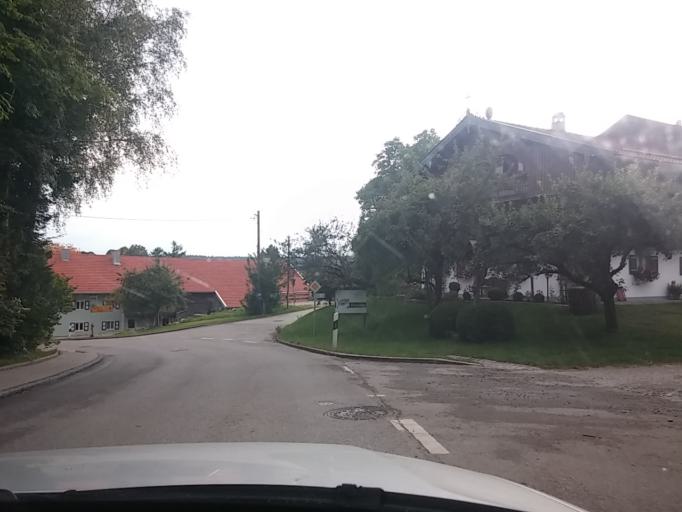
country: DE
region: Bavaria
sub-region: Upper Bavaria
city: Reichertshausen
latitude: 47.8902
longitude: 11.5879
